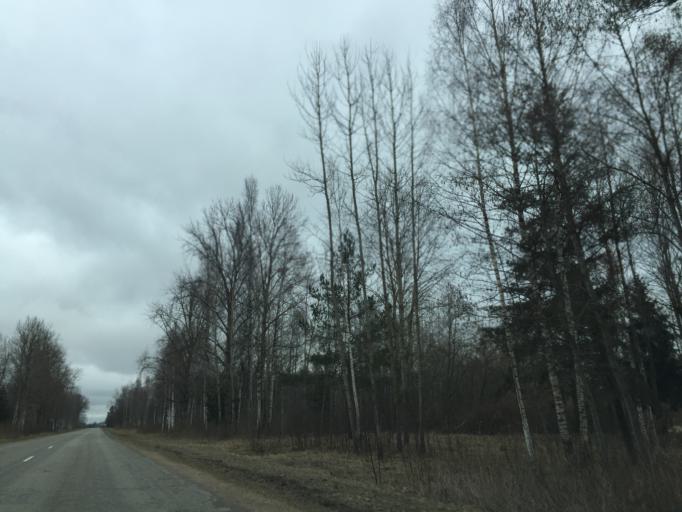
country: LV
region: Ilukste
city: Ilukste
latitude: 55.9677
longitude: 26.3046
